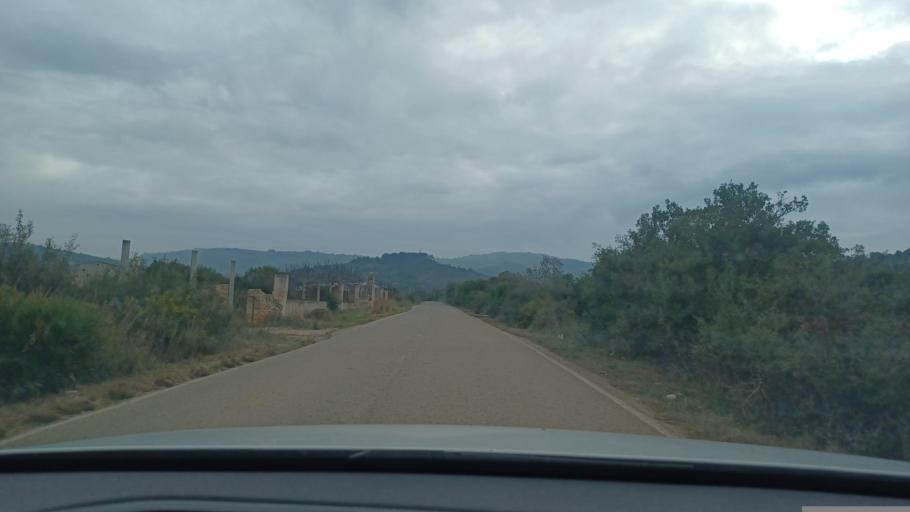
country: ES
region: Catalonia
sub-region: Provincia de Tarragona
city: Santa Barbara
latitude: 40.6631
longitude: 0.4581
